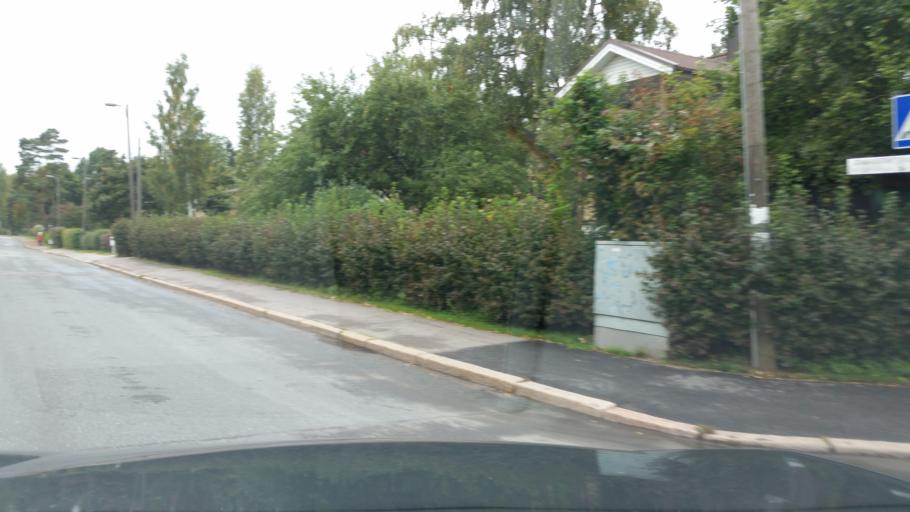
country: FI
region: Uusimaa
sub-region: Helsinki
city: Helsinki
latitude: 60.2375
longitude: 24.9230
